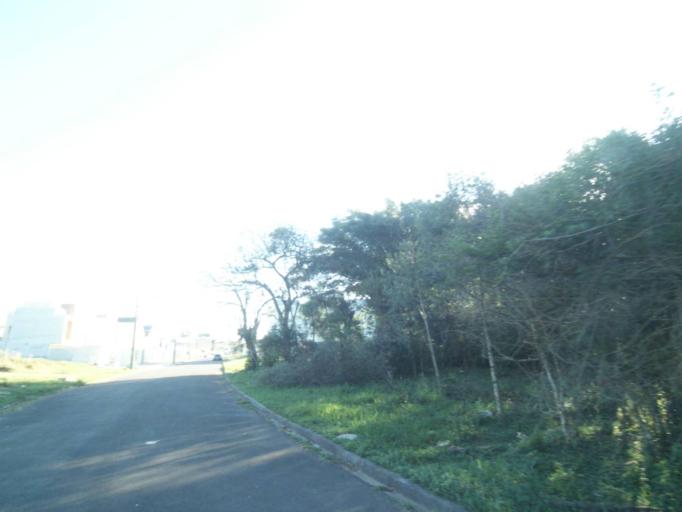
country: BR
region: Parana
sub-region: Curitiba
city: Curitiba
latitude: -25.3844
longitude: -49.2444
